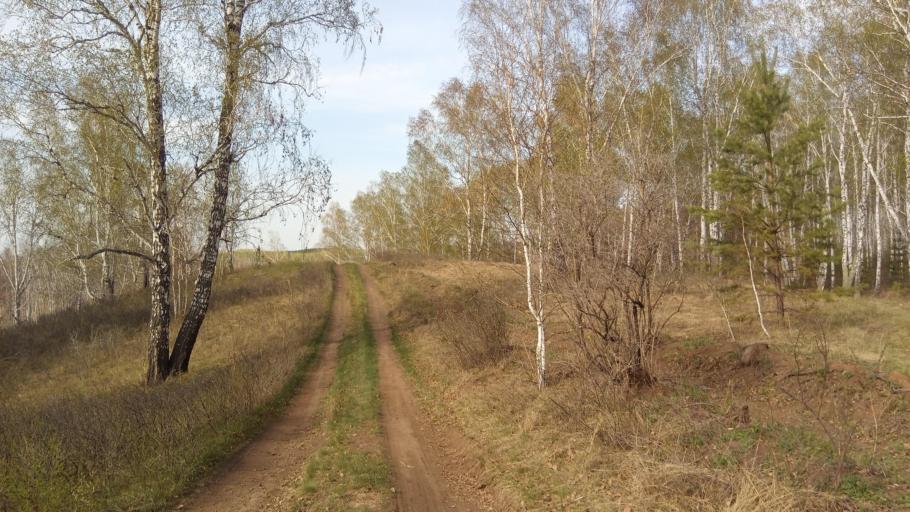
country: RU
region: Chelyabinsk
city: Poletayevo
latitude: 55.0306
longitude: 61.0738
